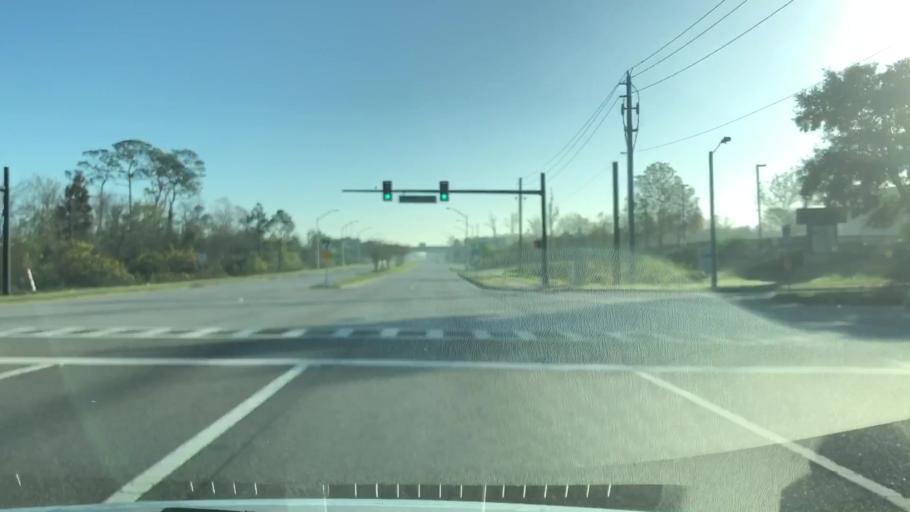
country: US
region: Florida
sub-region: Seminole County
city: Lake Mary
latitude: 28.7864
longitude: -81.3058
